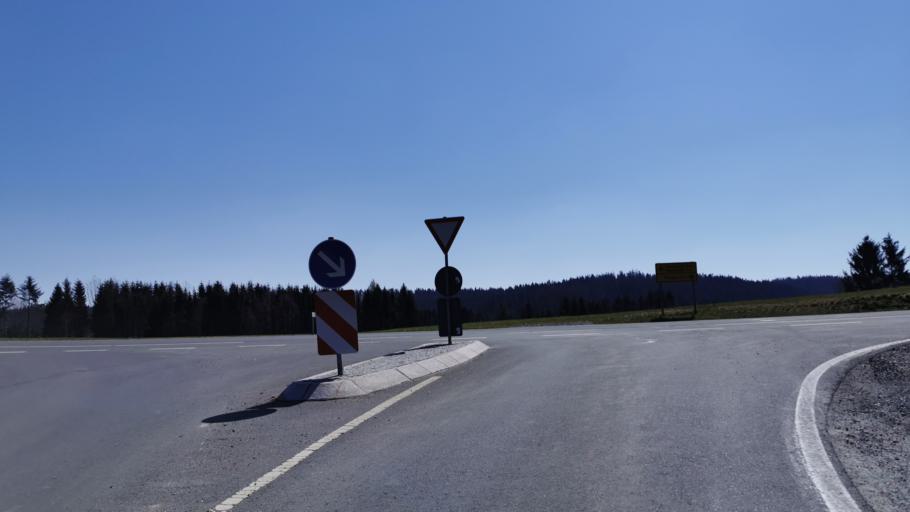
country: DE
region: Bavaria
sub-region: Upper Franconia
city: Pressig
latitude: 50.3591
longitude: 11.3413
